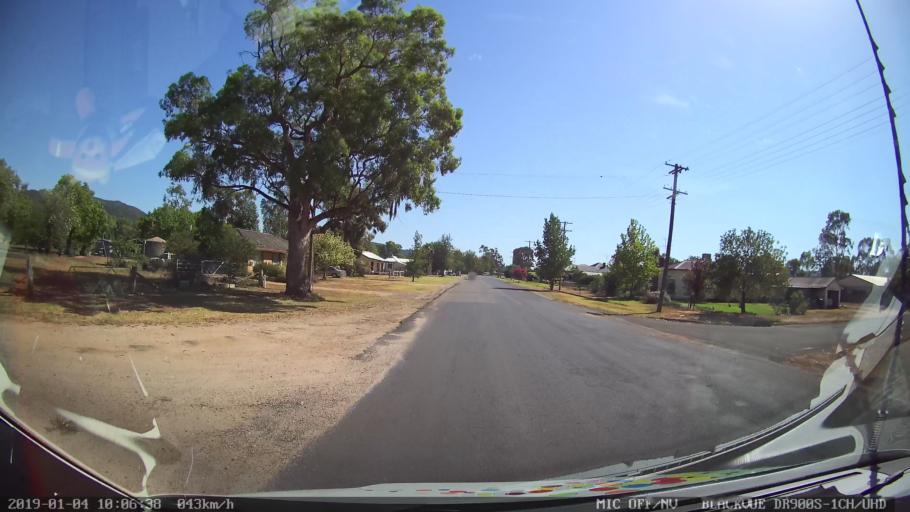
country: AU
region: New South Wales
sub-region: Cabonne
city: Canowindra
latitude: -33.4328
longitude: 148.3692
